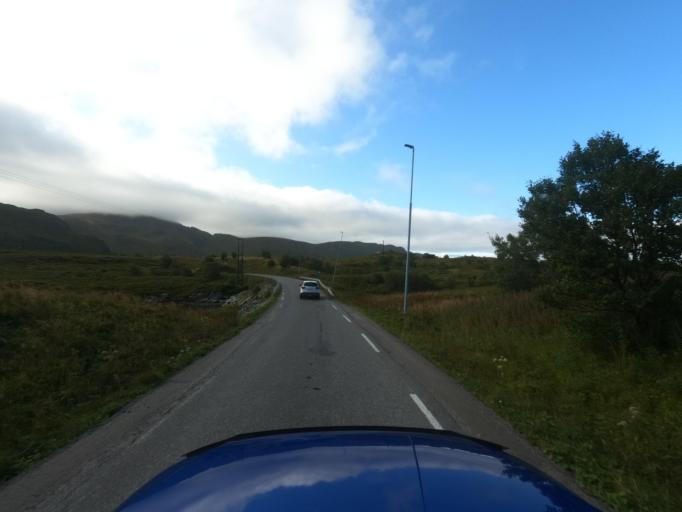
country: NO
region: Nordland
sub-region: Flakstad
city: Ramberg
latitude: 68.0868
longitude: 13.1804
